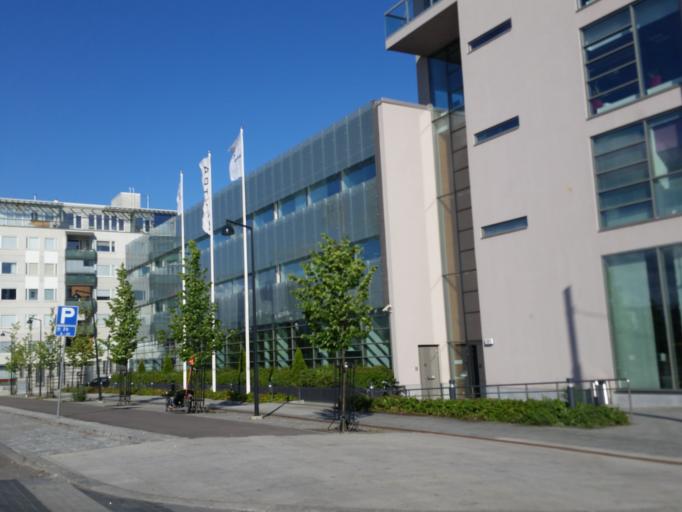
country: FI
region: Uusimaa
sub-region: Helsinki
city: Helsinki
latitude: 60.1597
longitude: 24.9091
